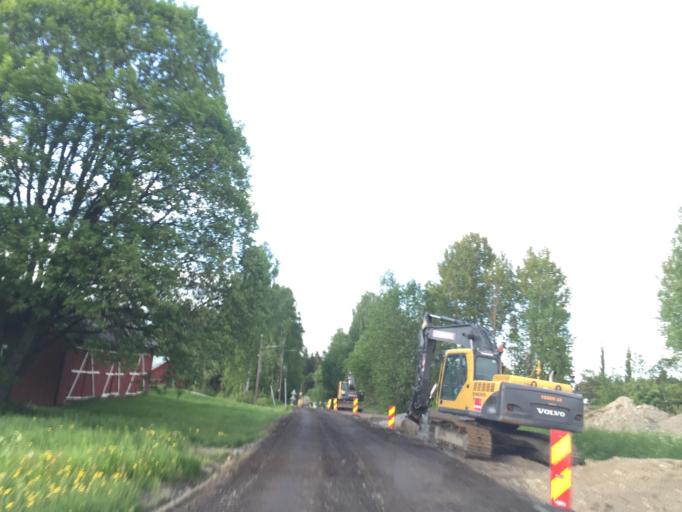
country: NO
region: Akershus
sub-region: Nes
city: Auli
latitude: 60.0237
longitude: 11.3290
